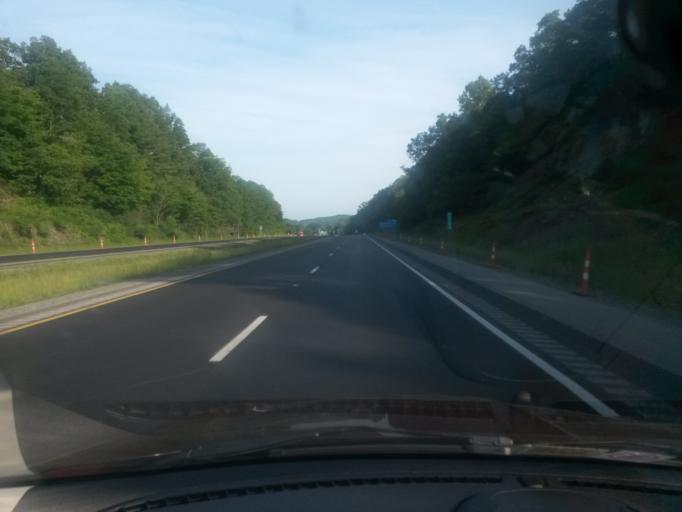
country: US
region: West Virginia
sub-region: Greenbrier County
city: Lewisburg
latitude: 37.8118
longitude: -80.4179
